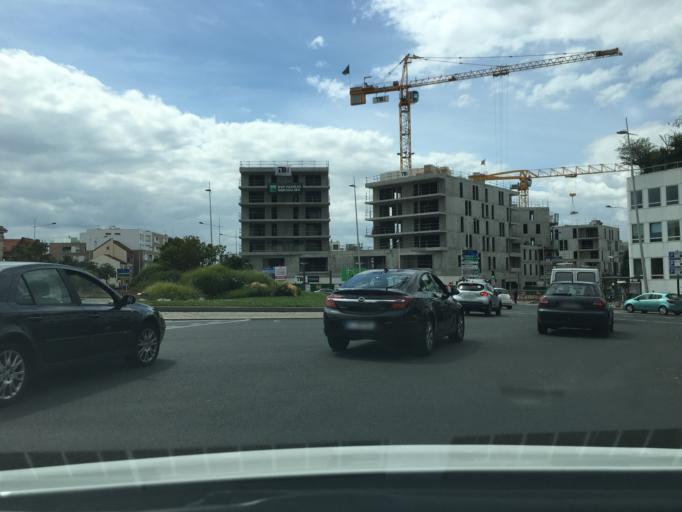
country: FR
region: Ile-de-France
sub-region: Departement des Hauts-de-Seine
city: Nanterre
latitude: 48.8874
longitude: 2.2007
